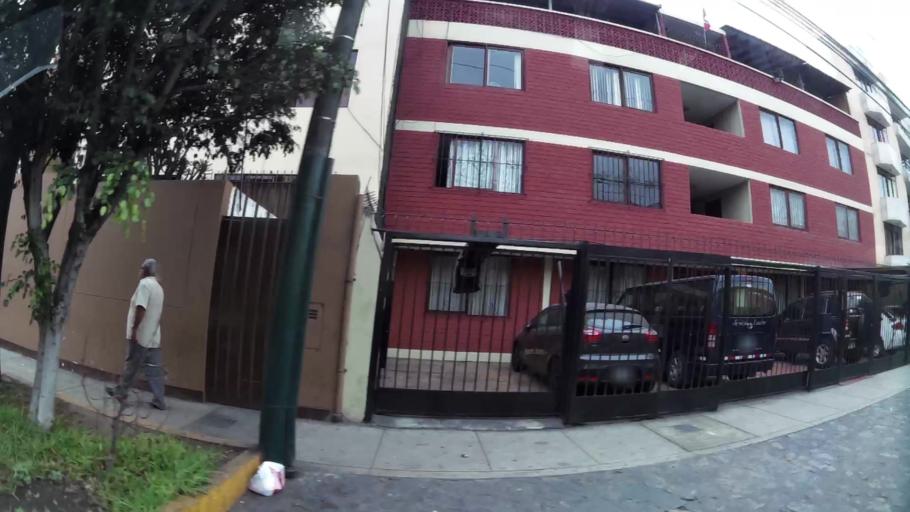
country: PE
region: Lima
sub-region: Lima
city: Surco
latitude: -12.1427
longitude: -77.0031
